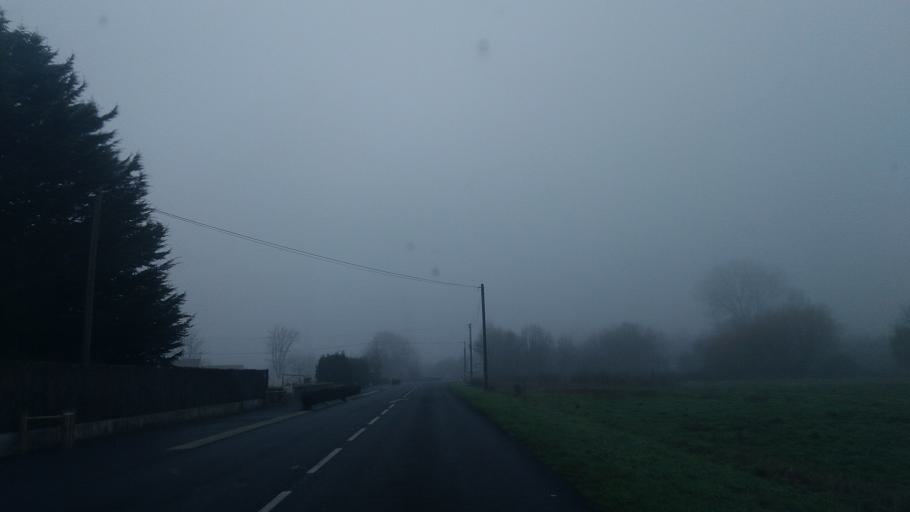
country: FR
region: Pays de la Loire
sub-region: Departement de la Vendee
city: Soullans
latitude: 46.8337
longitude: -1.9164
